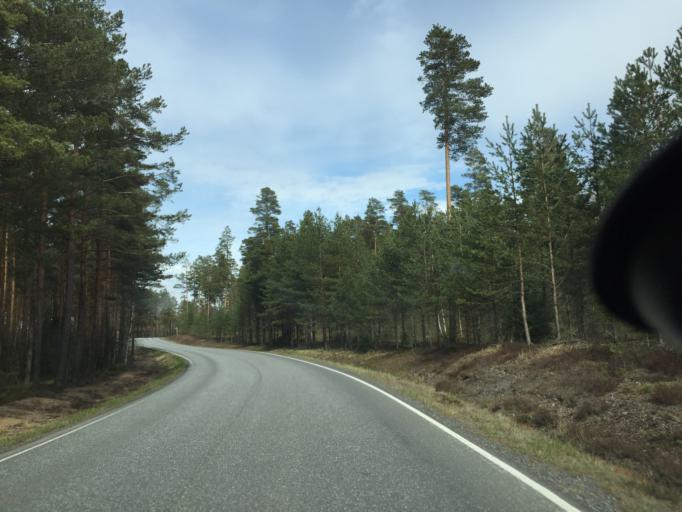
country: FI
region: Varsinais-Suomi
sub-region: Salo
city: Pernioe
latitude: 60.0209
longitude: 23.1731
